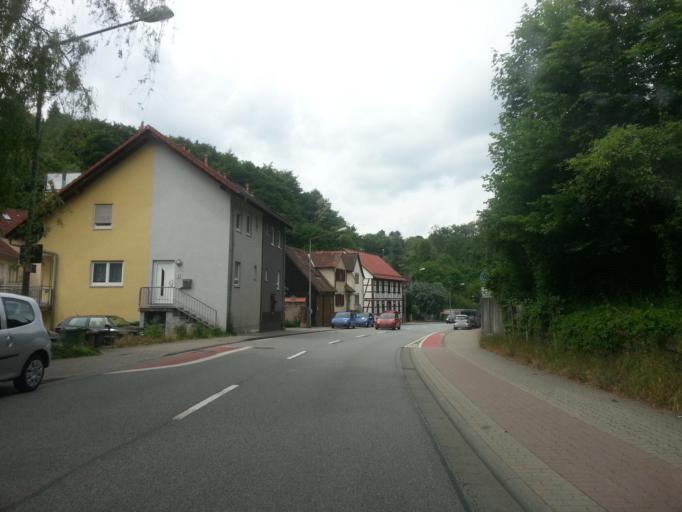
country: DE
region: Hesse
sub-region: Regierungsbezirk Darmstadt
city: Bensheim
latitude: 49.6934
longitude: 8.6536
